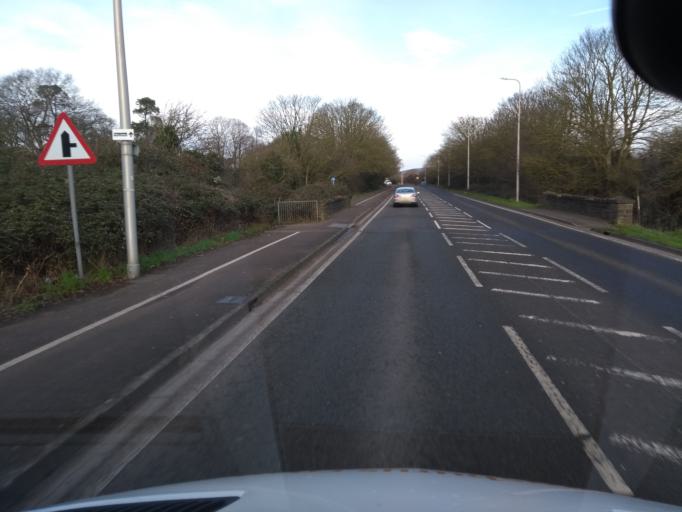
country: GB
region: England
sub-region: North Somerset
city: Weston-super-Mare
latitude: 51.3257
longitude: -2.9717
